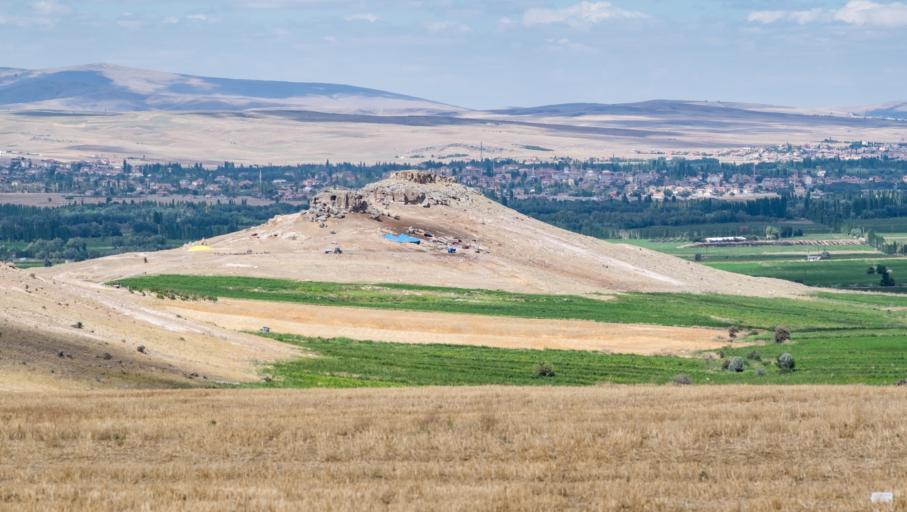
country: TR
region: Aksaray
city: Guzelyurt
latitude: 38.3072
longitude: 34.3247
